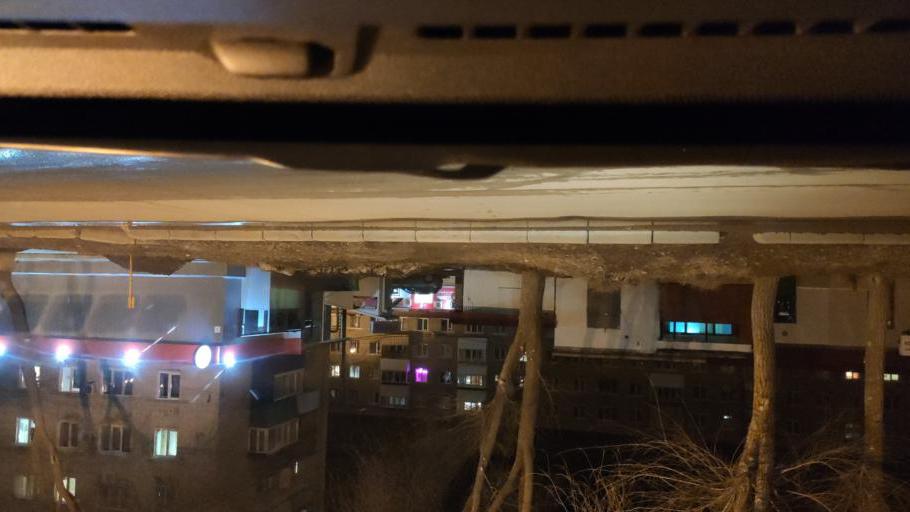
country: RU
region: Samara
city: Bereza
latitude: 53.5171
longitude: 50.1395
